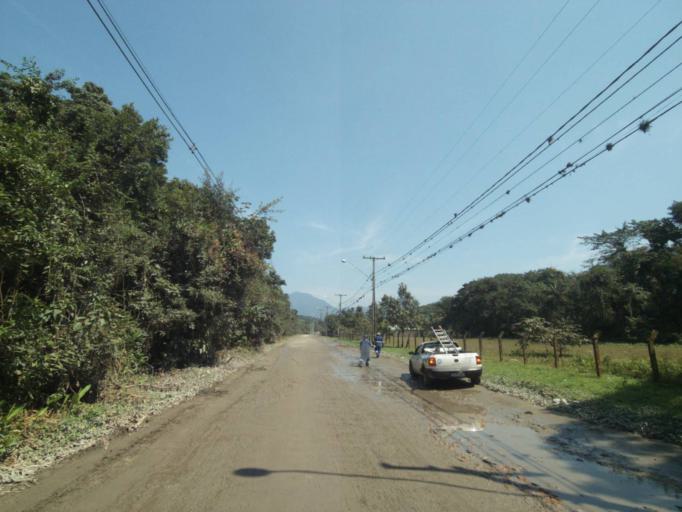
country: BR
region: Parana
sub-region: Paranagua
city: Paranagua
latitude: -25.5510
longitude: -48.5868
